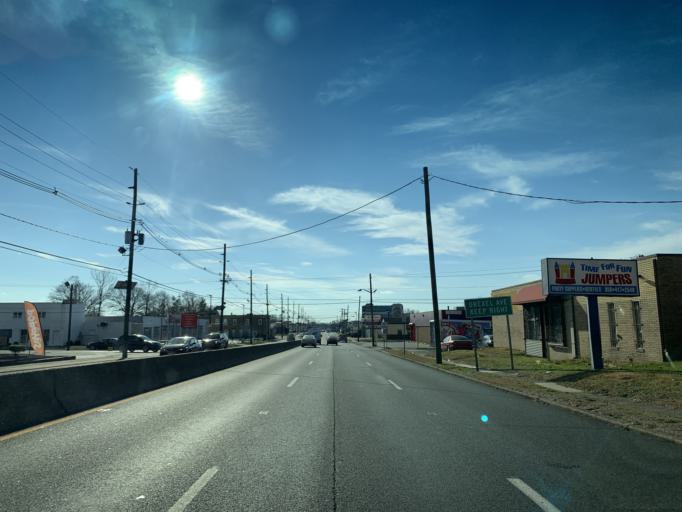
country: US
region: New Jersey
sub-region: Camden County
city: Merchantville
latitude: 39.9440
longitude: -75.0704
